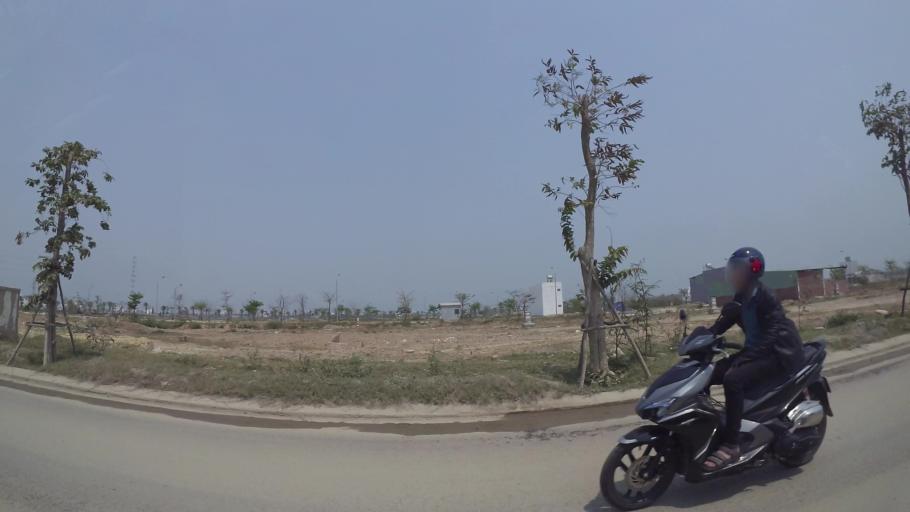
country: VN
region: Da Nang
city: Ngu Hanh Son
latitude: 16.0135
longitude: 108.2375
